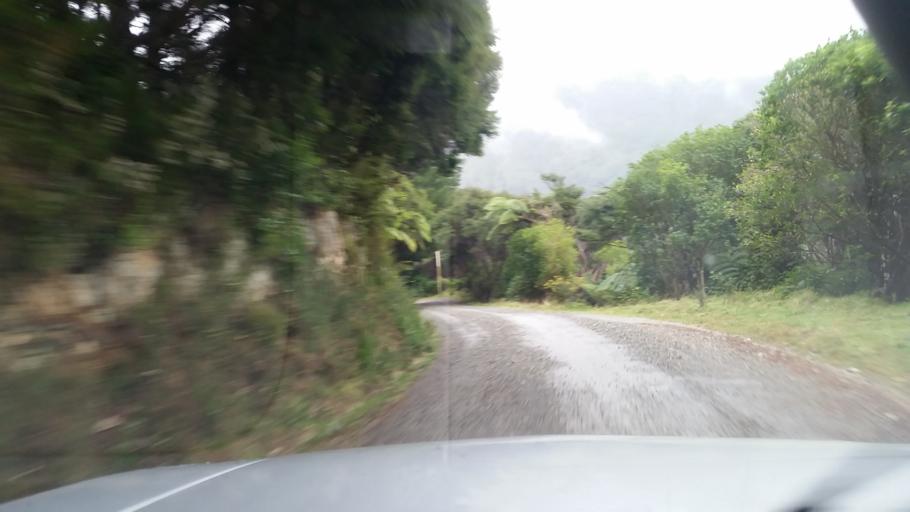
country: NZ
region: Marlborough
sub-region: Marlborough District
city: Picton
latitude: -41.1334
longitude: 174.0448
